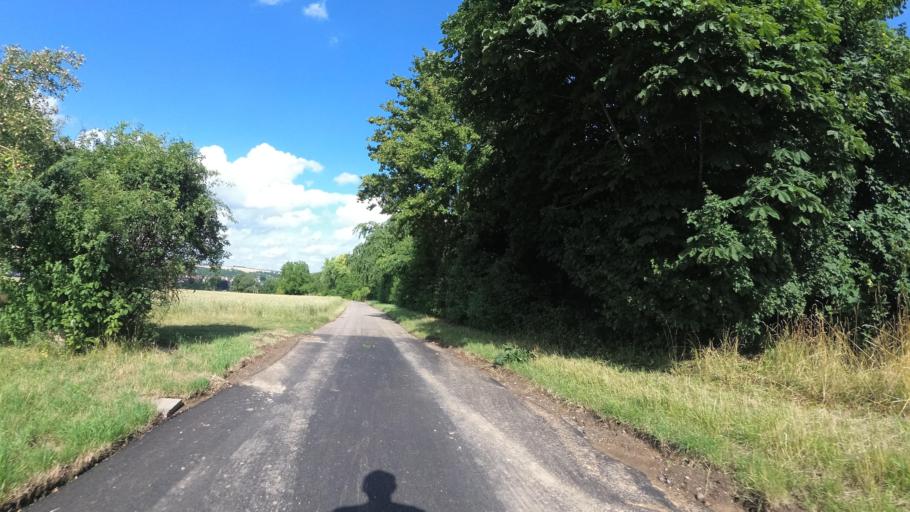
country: DE
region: Baden-Wuerttemberg
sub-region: Regierungsbezirk Stuttgart
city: Neuenstadt am Kocher
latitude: 49.2315
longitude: 9.3218
